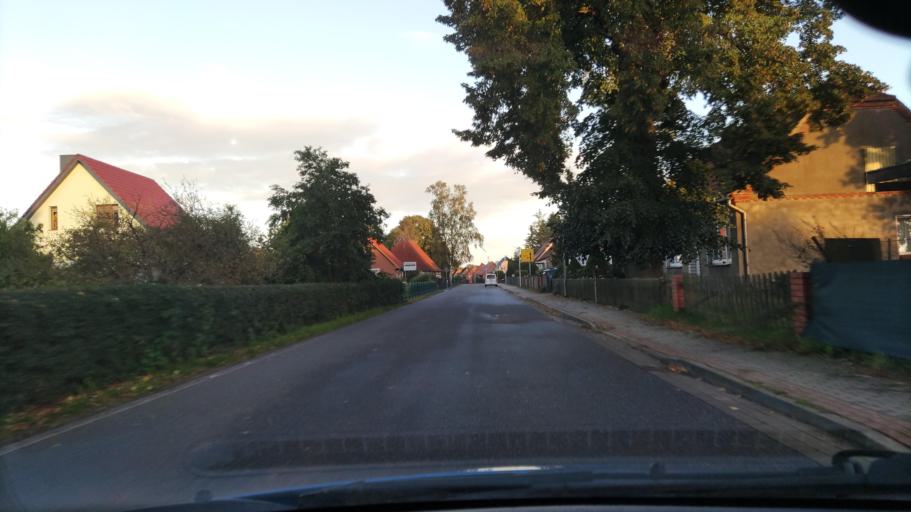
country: DE
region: Mecklenburg-Vorpommern
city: Lubtheen
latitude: 53.3187
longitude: 11.0178
